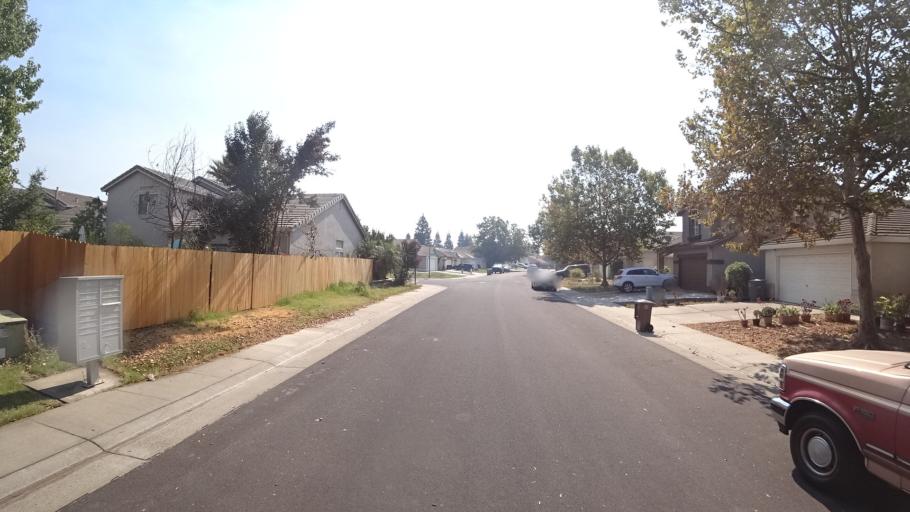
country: US
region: California
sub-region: Sacramento County
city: Laguna
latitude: 38.4282
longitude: -121.4162
